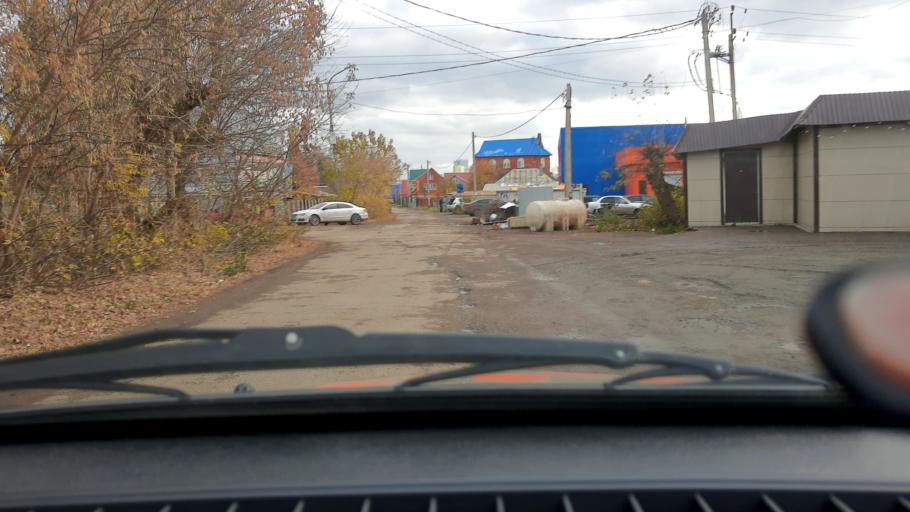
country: RU
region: Bashkortostan
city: Ufa
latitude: 54.7804
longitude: 56.0535
